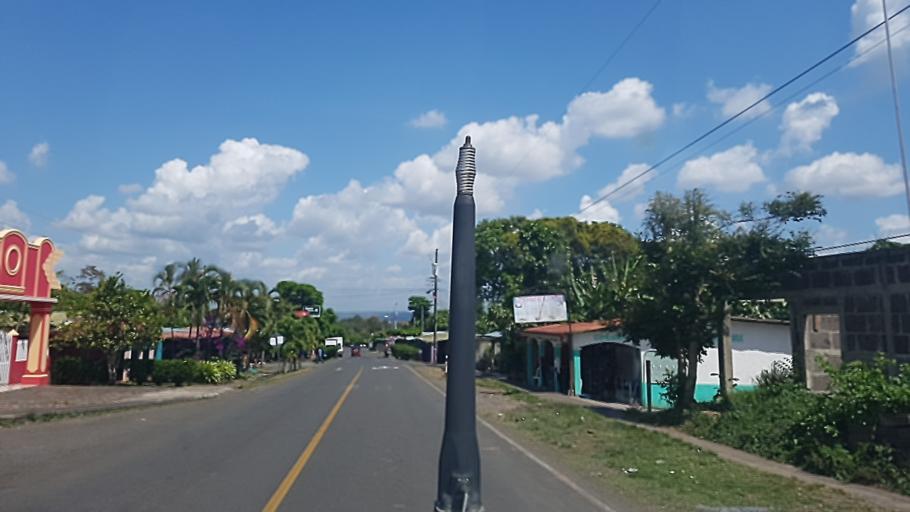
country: NI
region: Atlantico Sur
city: Muelle de los Bueyes
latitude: 11.9181
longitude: -84.6474
